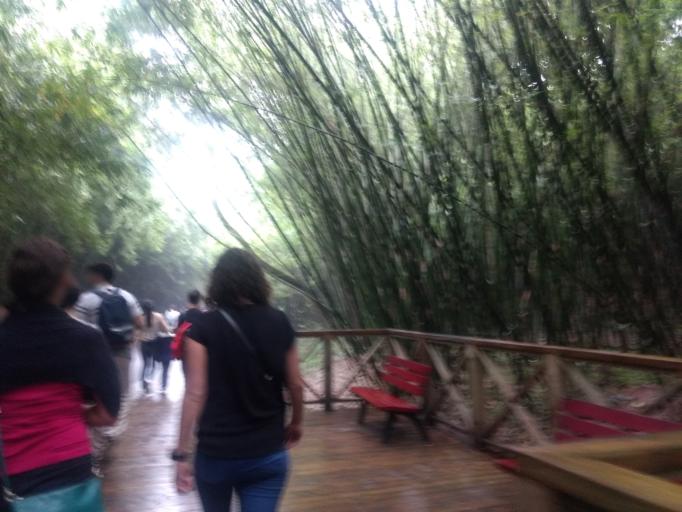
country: CN
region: Sichuan
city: Xindu
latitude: 30.7375
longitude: 104.1414
